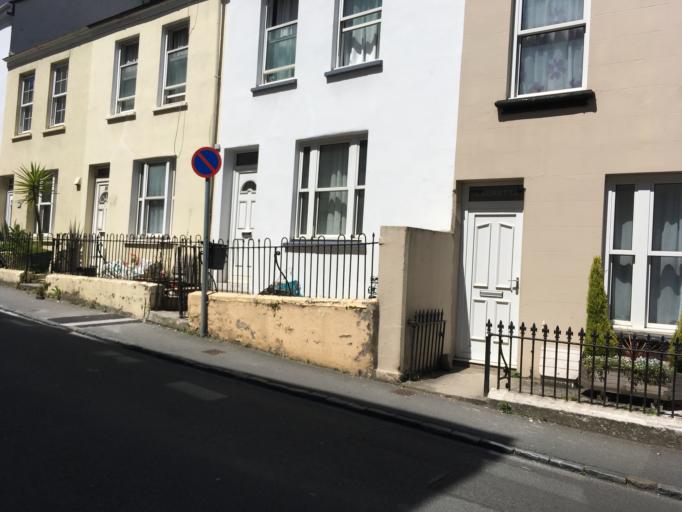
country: GG
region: St Peter Port
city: Saint Peter Port
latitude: 49.4532
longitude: -2.5426
